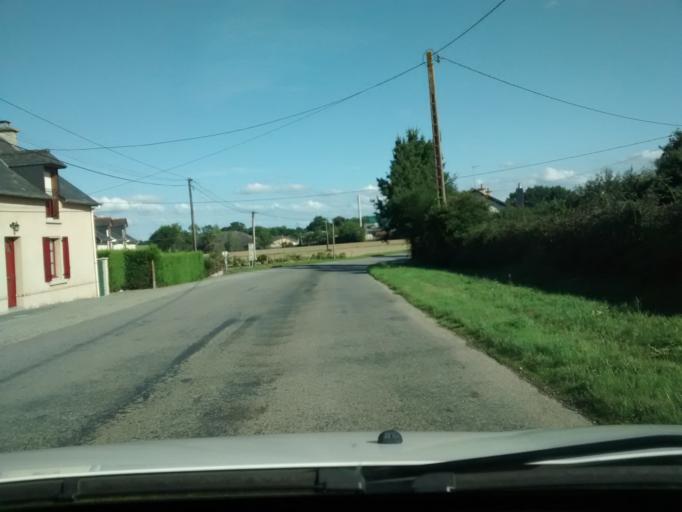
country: FR
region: Brittany
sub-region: Departement d'Ille-et-Vilaine
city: Nouvoitou
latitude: 48.0711
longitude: -1.5671
